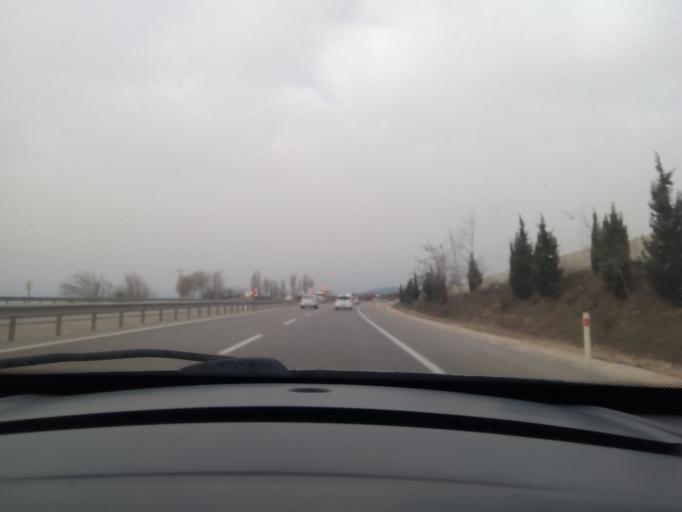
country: TR
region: Bursa
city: Mahmudiye
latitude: 40.2086
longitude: 28.5954
